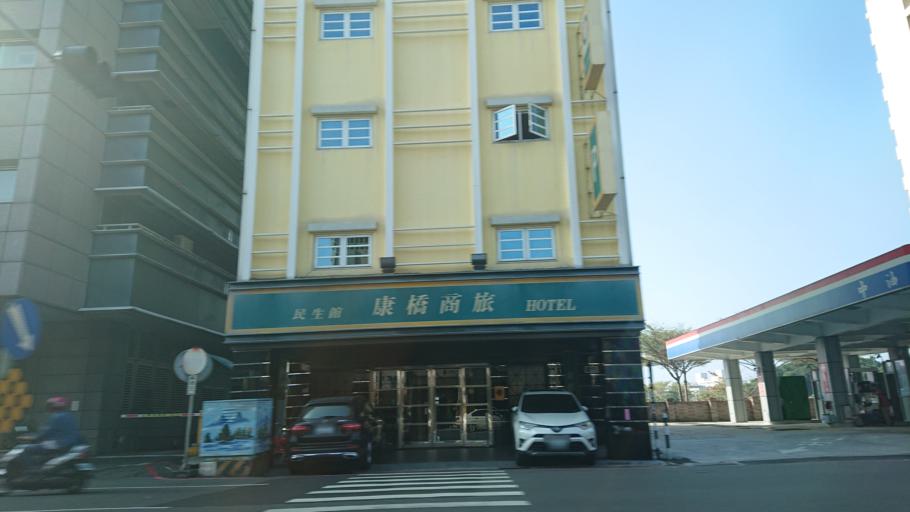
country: TW
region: Taiwan
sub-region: Tainan
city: Tainan
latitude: 22.9967
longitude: 120.1916
